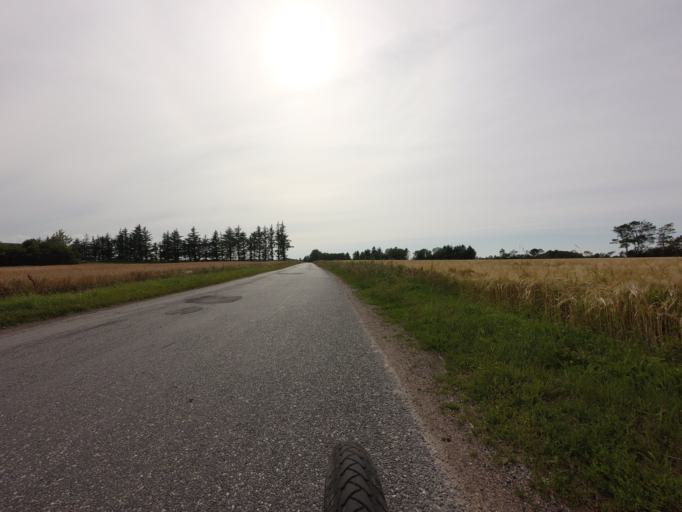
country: DK
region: North Denmark
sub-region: Hjorring Kommune
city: Hjorring
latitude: 57.4338
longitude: 9.9152
